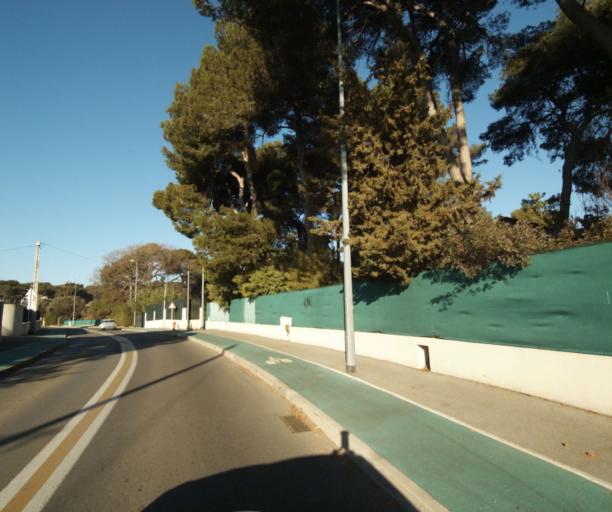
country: FR
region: Provence-Alpes-Cote d'Azur
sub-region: Departement des Alpes-Maritimes
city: Biot
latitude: 43.5962
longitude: 7.0860
